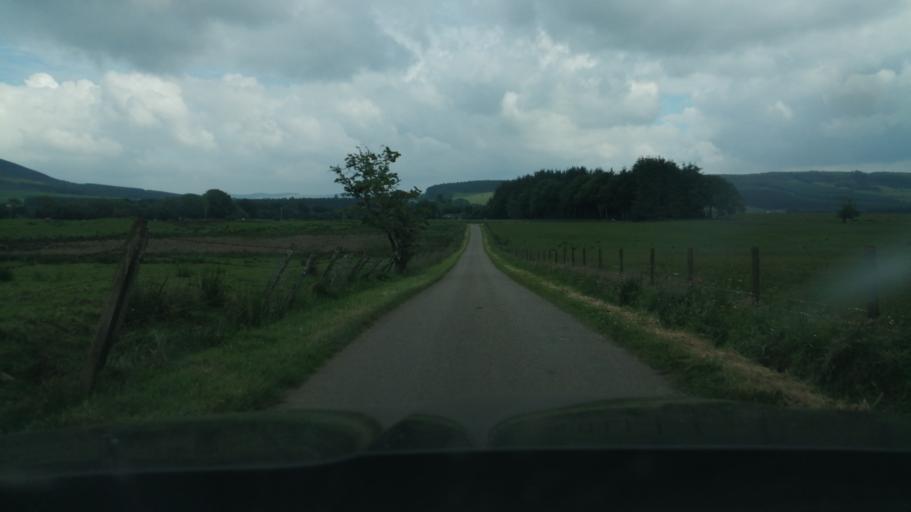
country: GB
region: Scotland
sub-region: Moray
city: Cullen
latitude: 57.5913
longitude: -2.8220
